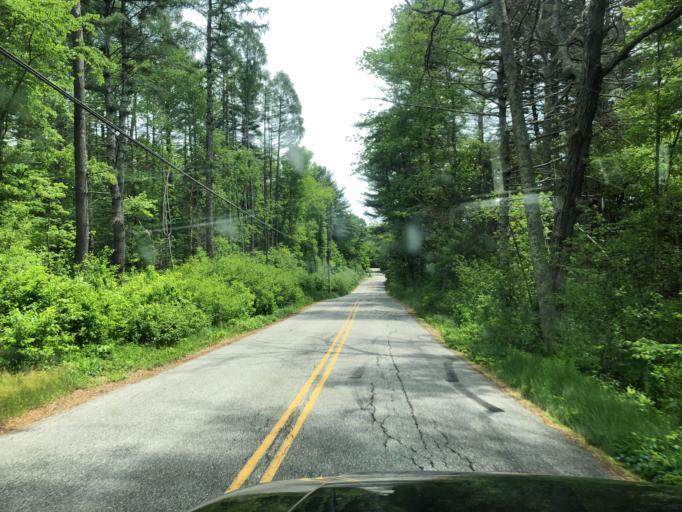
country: US
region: Connecticut
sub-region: Windham County
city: Thompson
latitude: 41.9647
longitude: -71.8273
